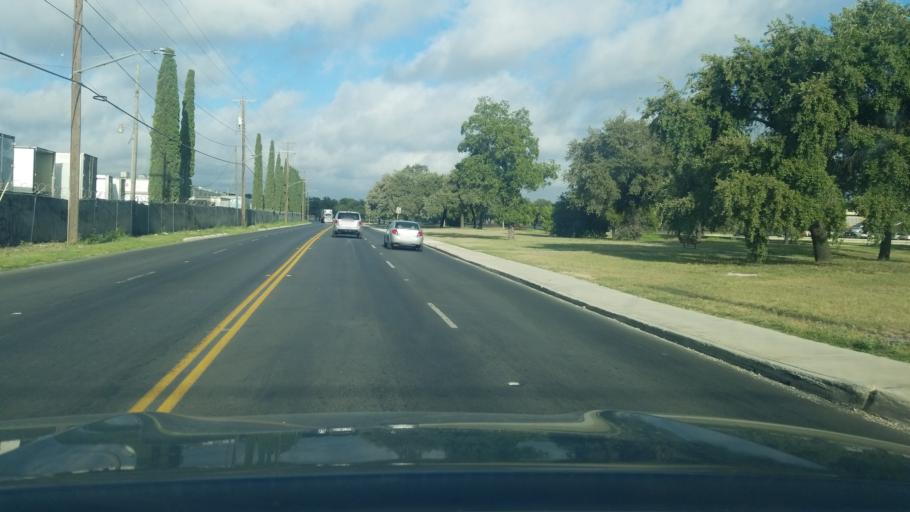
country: US
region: Texas
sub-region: Bexar County
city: San Antonio
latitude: 29.4129
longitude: -98.5244
